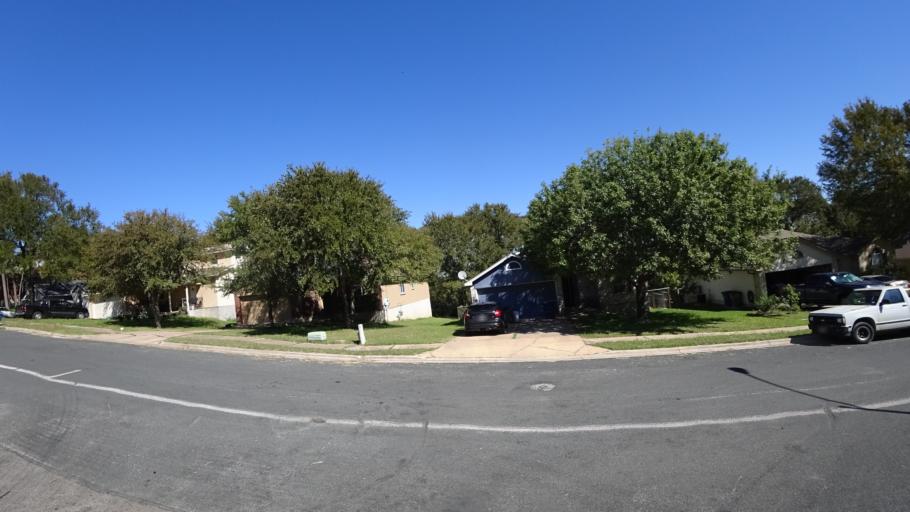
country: US
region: Texas
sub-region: Travis County
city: Austin
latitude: 30.2912
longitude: -97.6600
